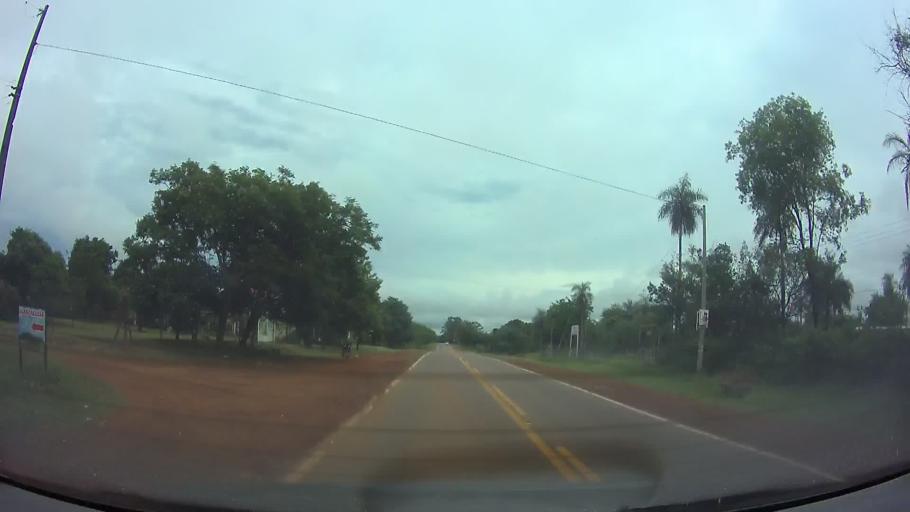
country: PY
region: Paraguari
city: Acahay
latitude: -25.8700
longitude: -57.1263
